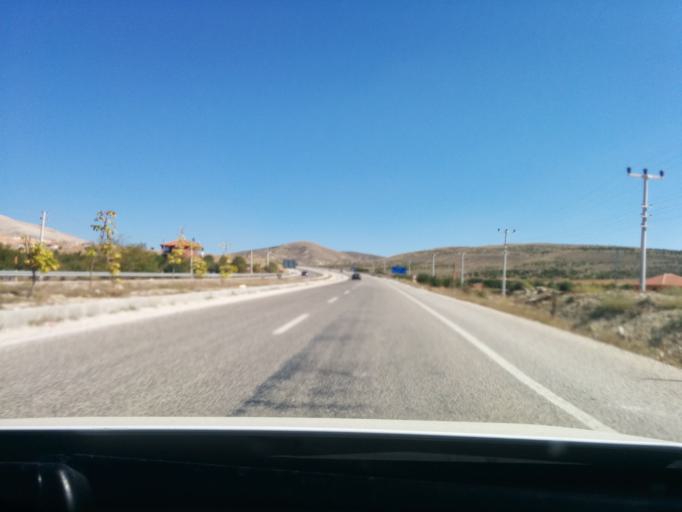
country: TR
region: Antalya
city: Kizilcadag
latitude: 37.0146
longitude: 29.9649
